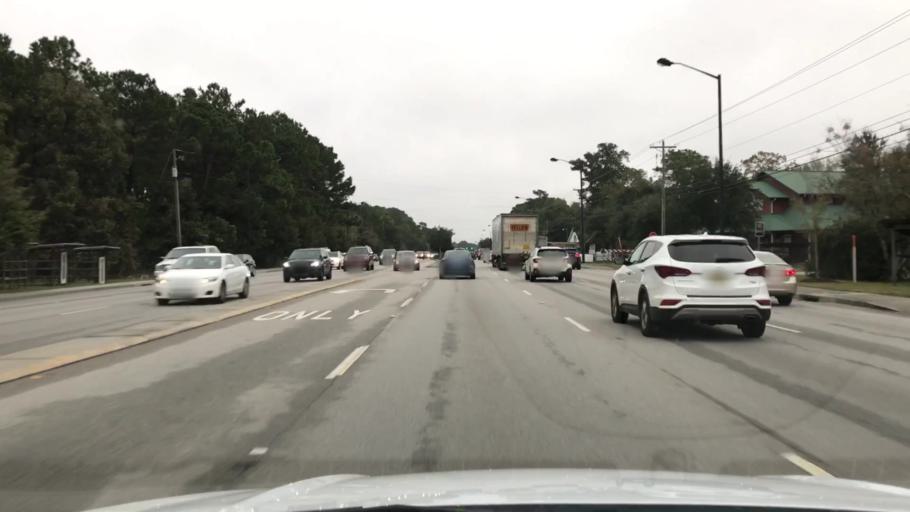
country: US
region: South Carolina
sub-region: Charleston County
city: Isle of Palms
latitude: 32.8505
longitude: -79.8062
